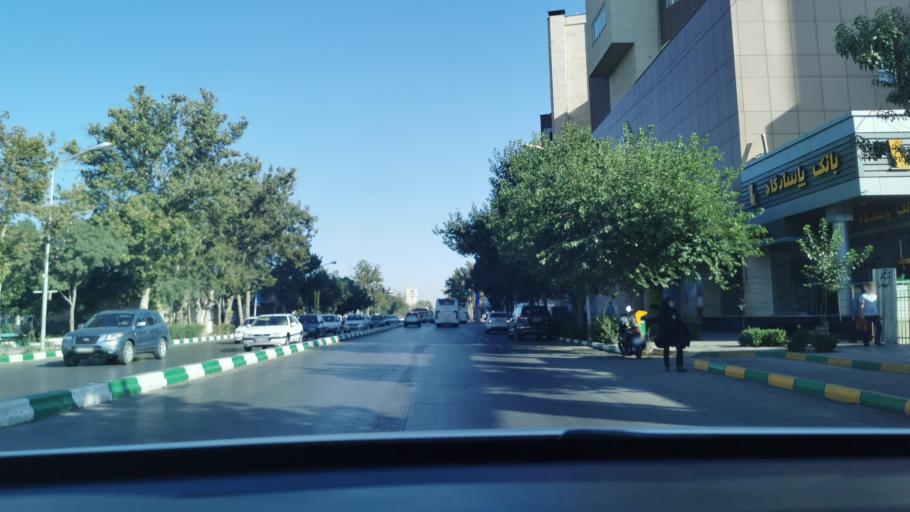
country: IR
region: Razavi Khorasan
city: Mashhad
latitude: 36.3116
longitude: 59.5914
